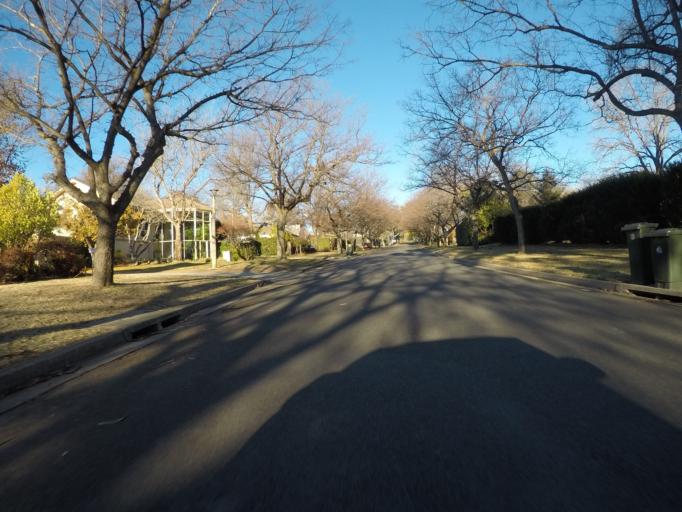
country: AU
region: Australian Capital Territory
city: Forrest
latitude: -35.3038
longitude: 149.1096
